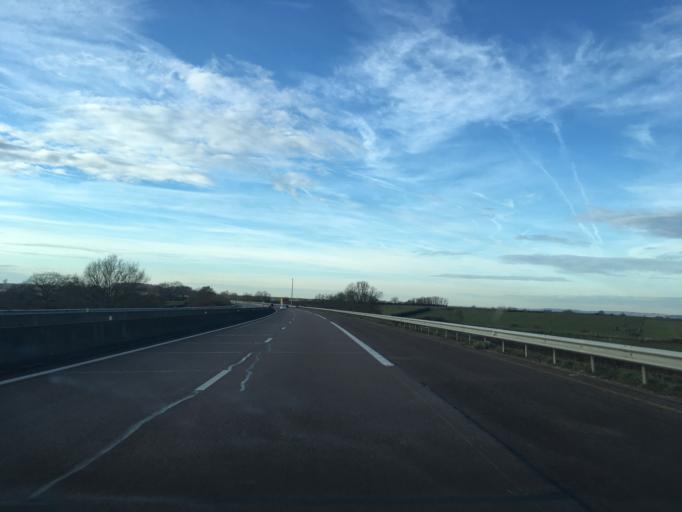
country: FR
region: Bourgogne
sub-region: Departement de la Cote-d'Or
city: Semur-en-Auxois
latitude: 47.4652
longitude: 4.2462
